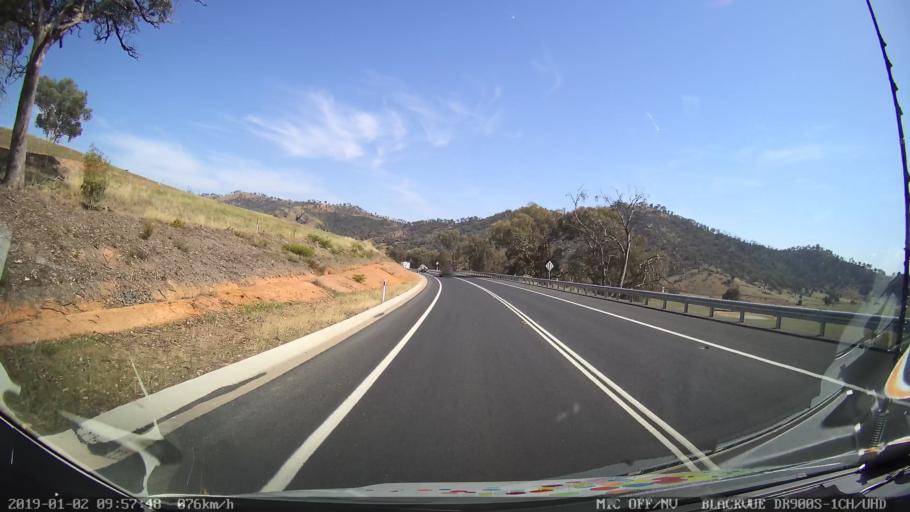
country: AU
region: New South Wales
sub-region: Tumut Shire
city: Tumut
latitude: -35.2012
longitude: 148.1648
